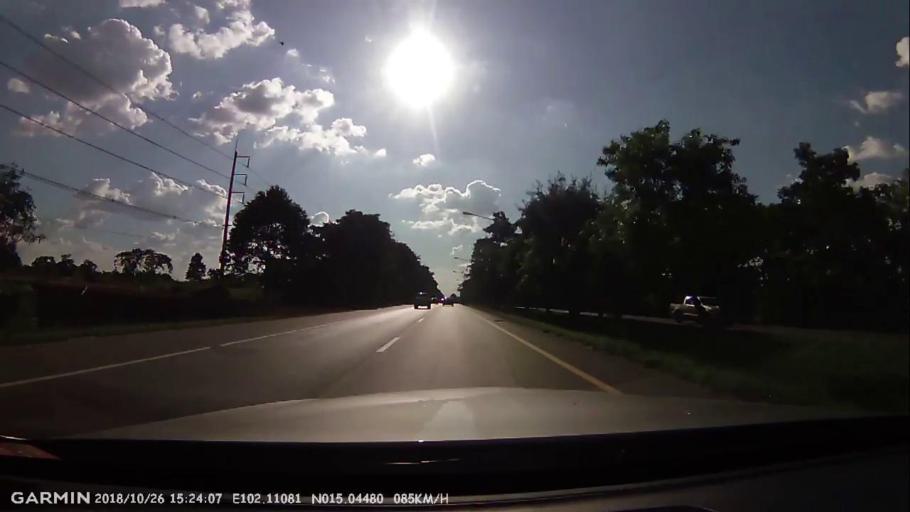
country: TH
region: Nakhon Ratchasima
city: Nakhon Ratchasima
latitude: 15.0448
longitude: 102.1109
